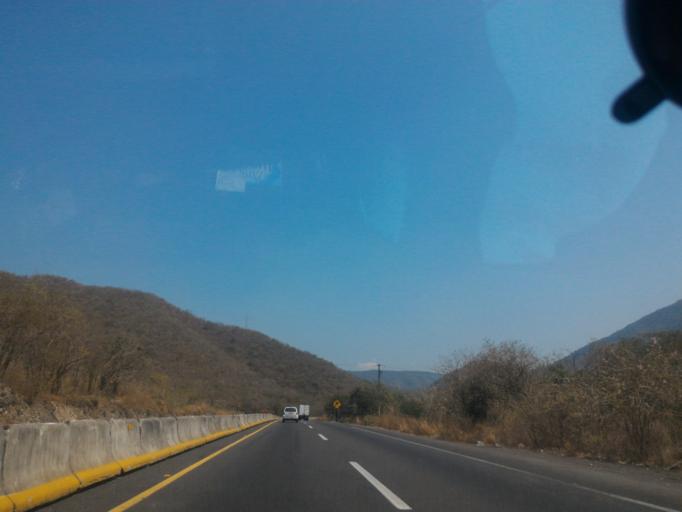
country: MX
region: Colima
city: Ixtlahuacan
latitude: 19.0222
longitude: -103.8158
